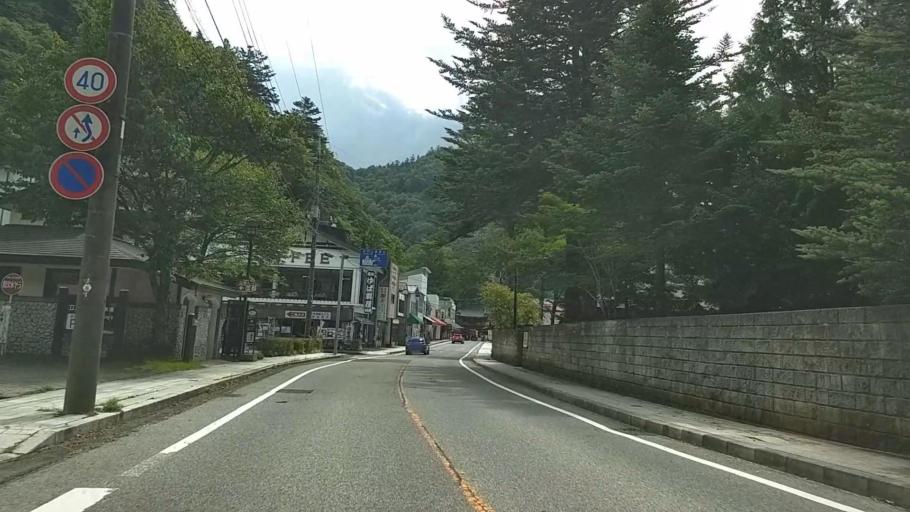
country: JP
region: Tochigi
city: Nikko
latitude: 36.7335
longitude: 139.4924
